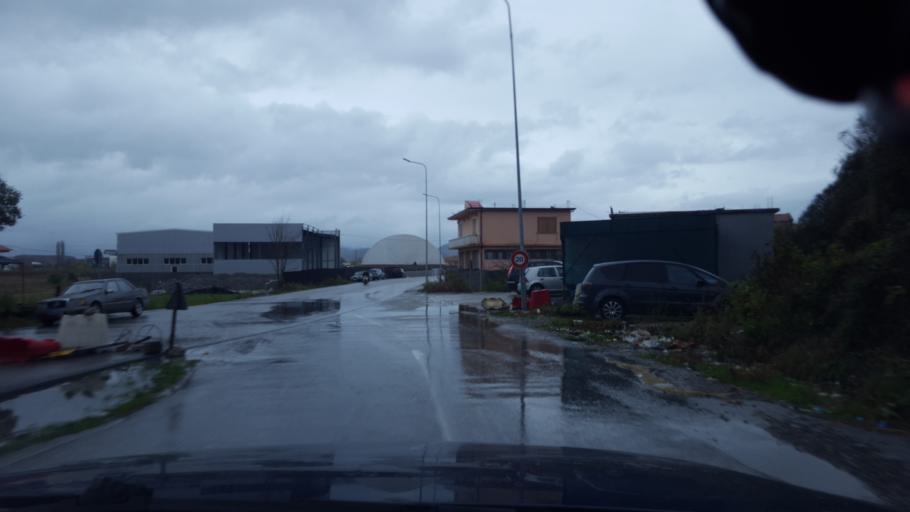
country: AL
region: Shkoder
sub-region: Rrethi i Shkodres
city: Berdica e Madhe
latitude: 42.0307
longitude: 19.4973
